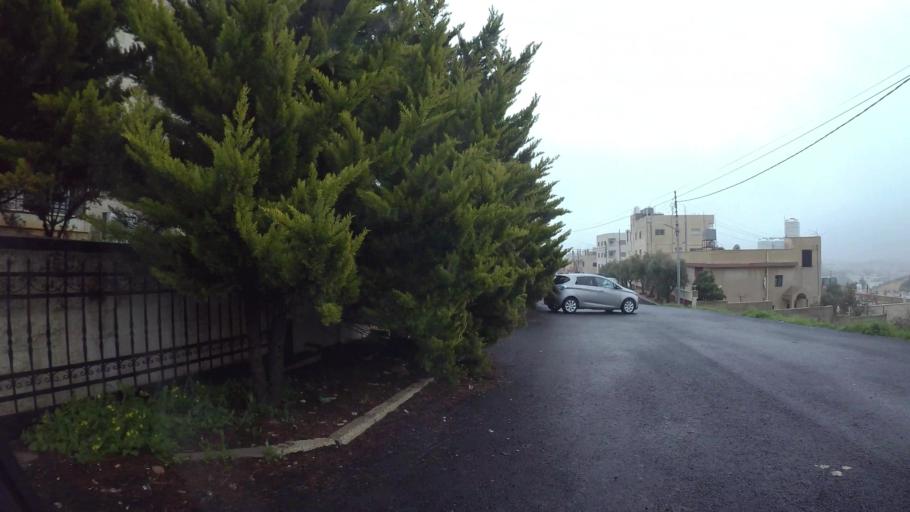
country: JO
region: Amman
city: Al Jubayhah
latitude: 32.0216
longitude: 35.8324
